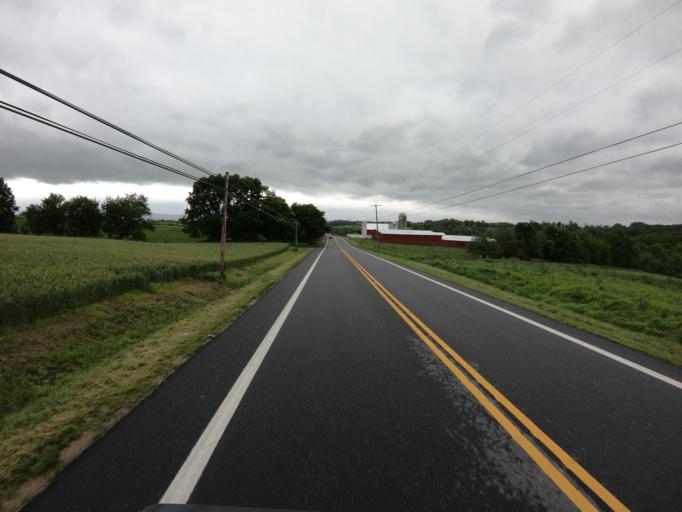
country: US
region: Maryland
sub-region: Frederick County
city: Myersville
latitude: 39.4731
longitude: -77.6029
